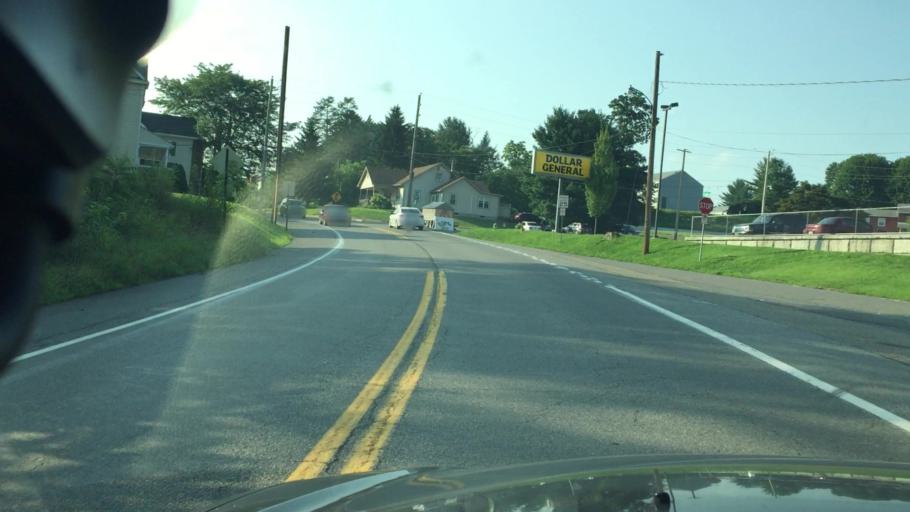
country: US
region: Pennsylvania
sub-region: Columbia County
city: Catawissa
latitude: 40.9480
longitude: -76.4564
